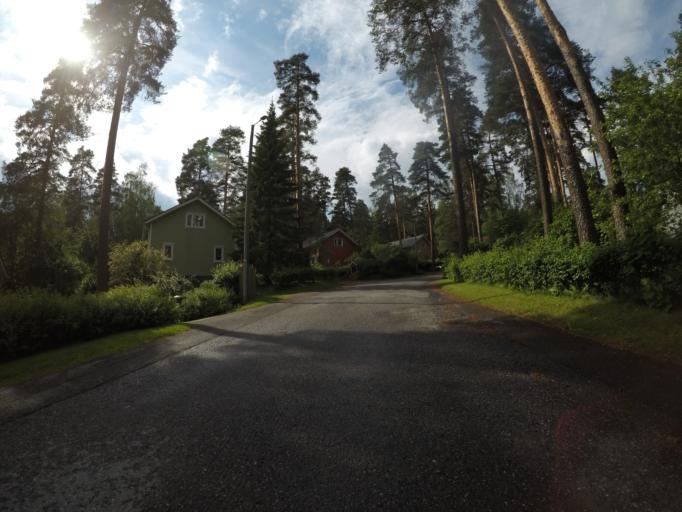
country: FI
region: Haeme
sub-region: Haemeenlinna
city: Haemeenlinna
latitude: 61.0137
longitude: 24.4661
